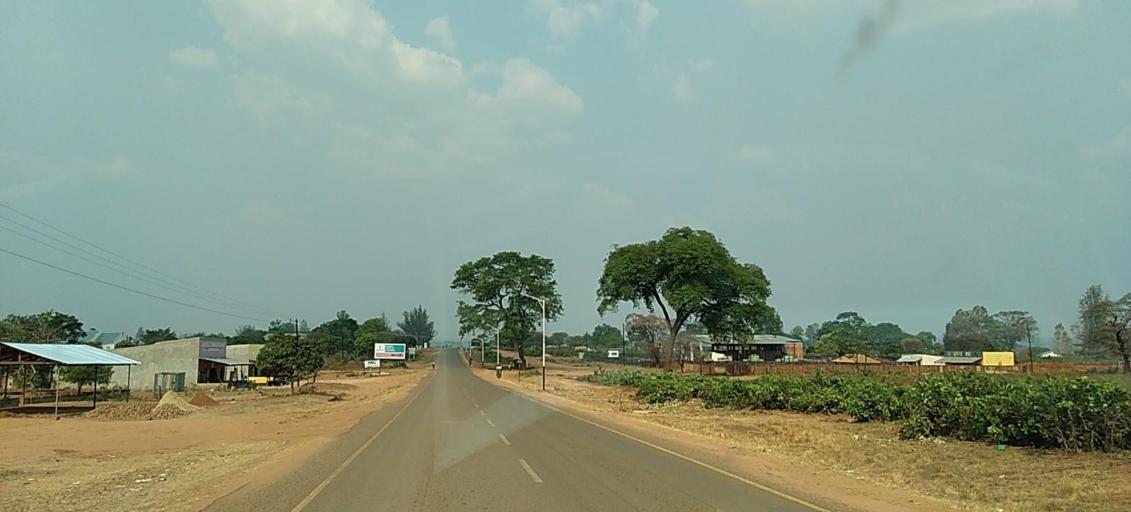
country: ZM
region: North-Western
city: Kabompo
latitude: -13.5931
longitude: 24.2039
